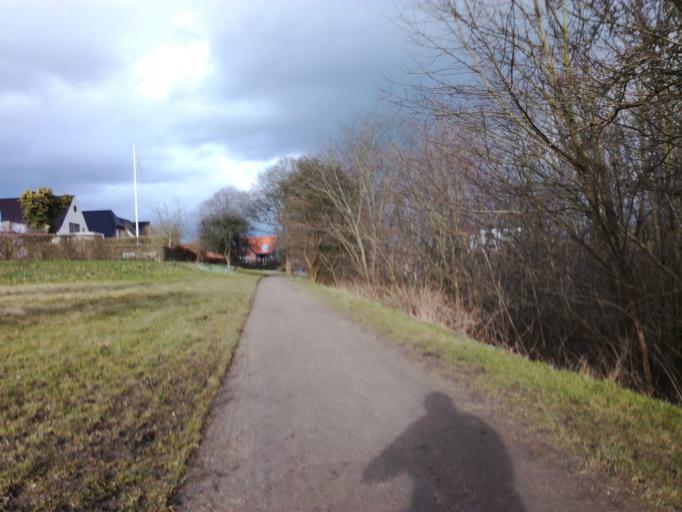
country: DK
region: South Denmark
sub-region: Fredericia Kommune
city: Fredericia
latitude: 55.5715
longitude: 9.7648
